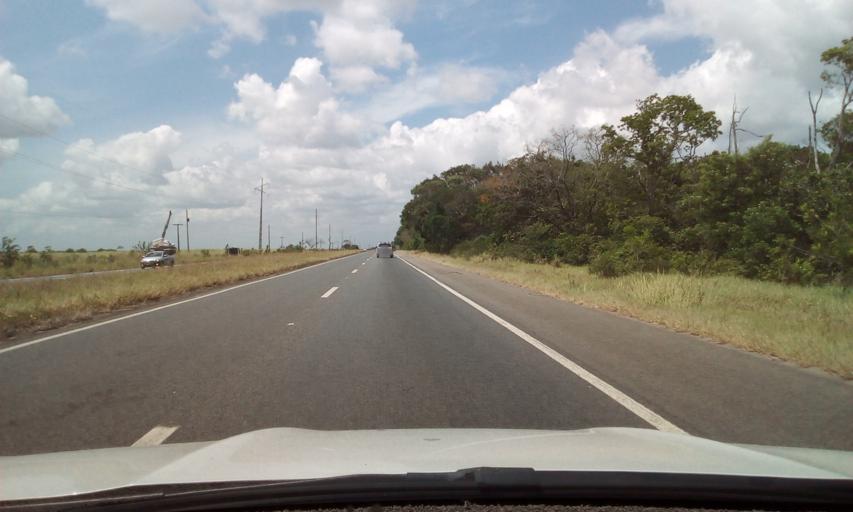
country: BR
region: Paraiba
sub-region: Santa Rita
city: Santa Rita
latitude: -7.1574
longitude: -35.0164
